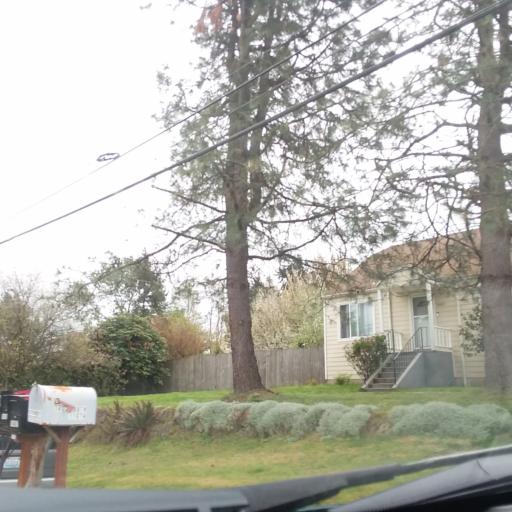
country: US
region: Washington
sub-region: King County
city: Boulevard Park
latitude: 47.4994
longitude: -122.3150
